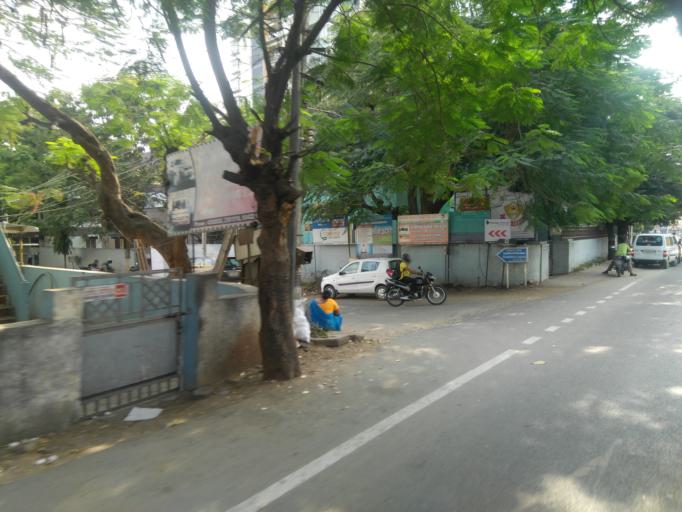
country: IN
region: Tamil Nadu
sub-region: Coimbatore
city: Coimbatore
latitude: 10.9954
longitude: 76.9754
